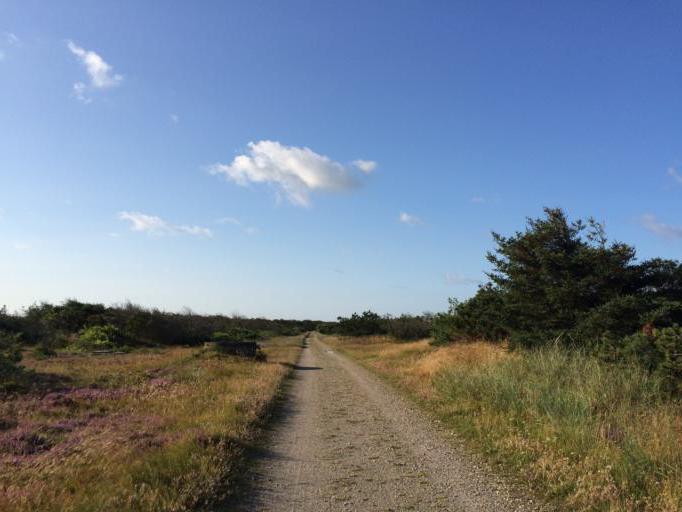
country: DK
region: Central Jutland
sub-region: Holstebro Kommune
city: Ulfborg
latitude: 56.3148
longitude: 8.1323
